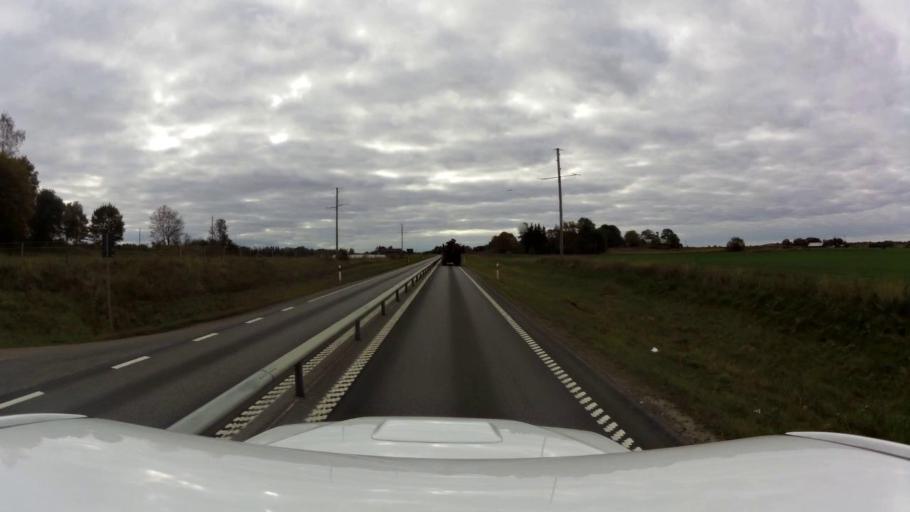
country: SE
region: OEstergoetland
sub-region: Linkopings Kommun
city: Malmslatt
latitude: 58.3431
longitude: 15.5531
